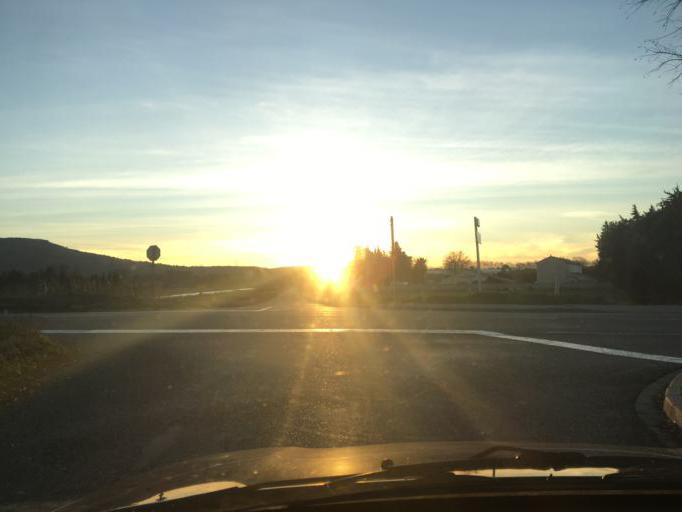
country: FR
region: Provence-Alpes-Cote d'Azur
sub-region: Departement des Bouches-du-Rhone
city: Mallemort
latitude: 43.7223
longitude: 5.1822
